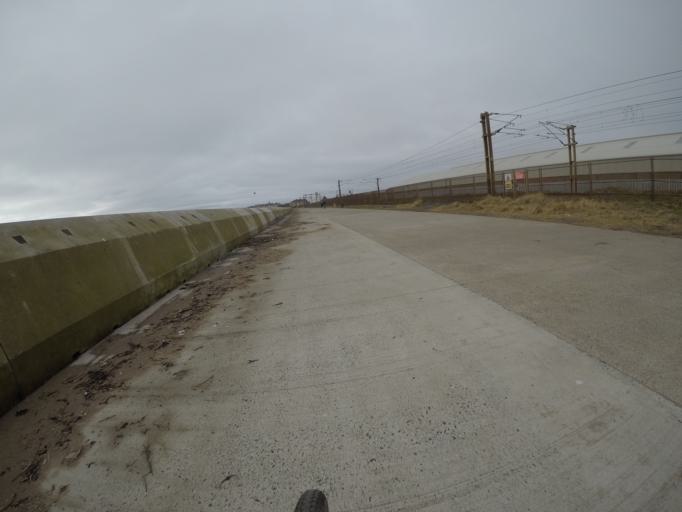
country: GB
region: Scotland
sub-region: North Ayrshire
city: Saltcoats
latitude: 55.6329
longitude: -4.7723
